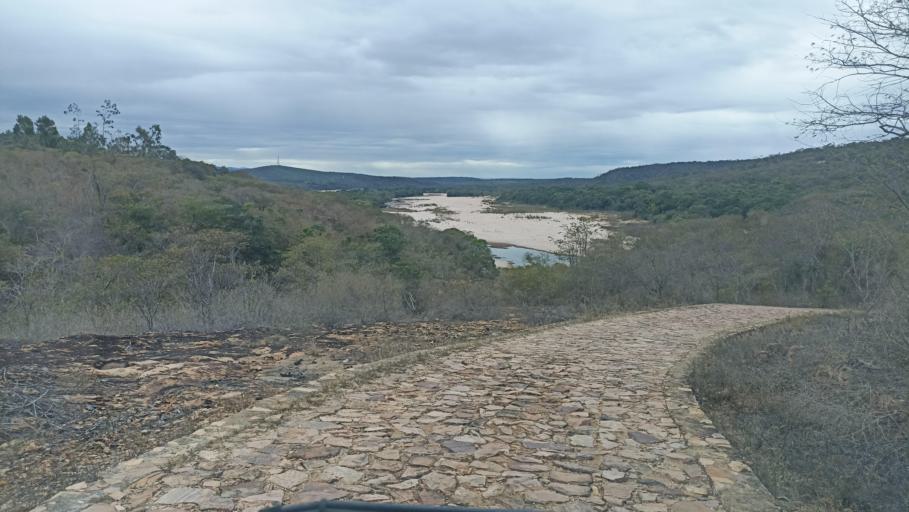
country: BR
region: Bahia
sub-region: Andarai
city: Vera Cruz
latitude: -12.8556
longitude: -41.3117
